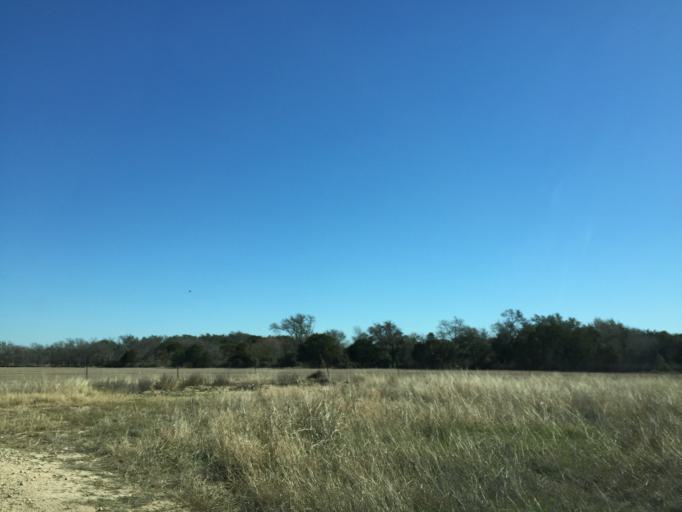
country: US
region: Texas
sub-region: Williamson County
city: Leander
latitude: 30.5748
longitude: -97.8683
